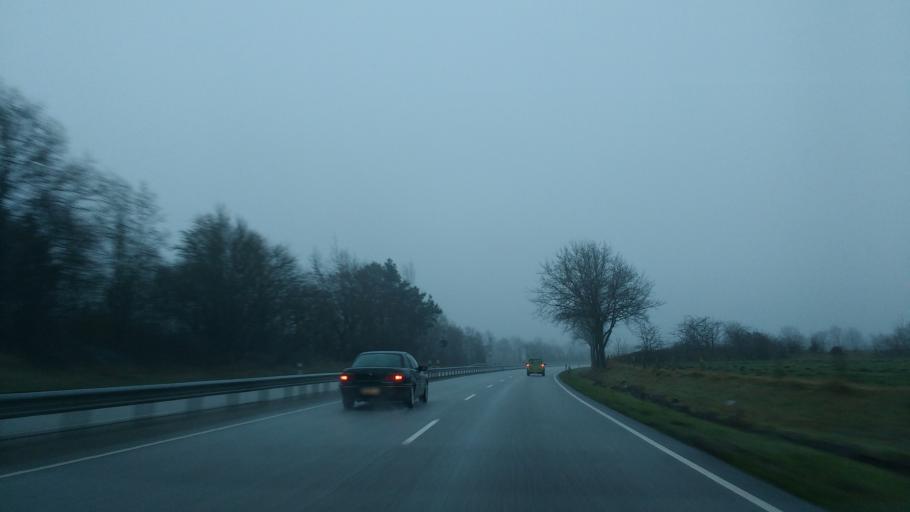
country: DE
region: Schleswig-Holstein
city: Westerronfeld
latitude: 54.2715
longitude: 9.6663
